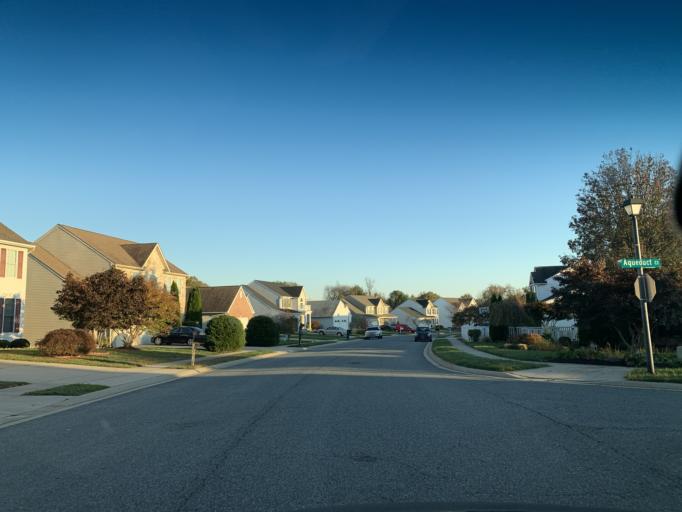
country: US
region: Maryland
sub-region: Harford County
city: Bel Air North
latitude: 39.5674
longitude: -76.3781
